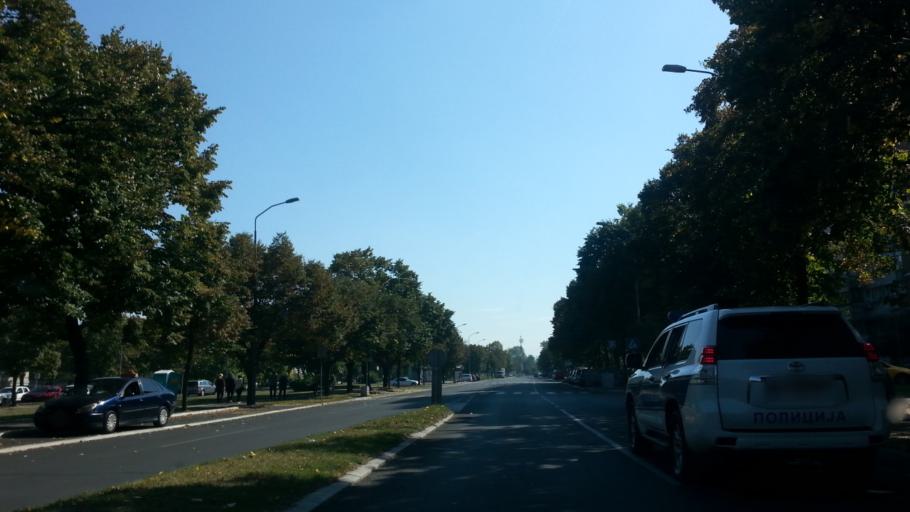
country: RS
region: Central Serbia
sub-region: Belgrade
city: Cukarica
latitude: 44.8002
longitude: 20.3818
